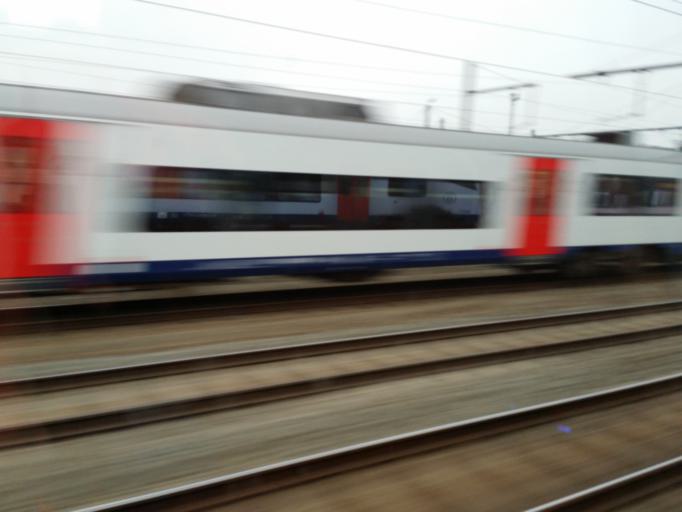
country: BE
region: Flanders
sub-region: Provincie Oost-Vlaanderen
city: Ledeberg
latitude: 51.0229
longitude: 3.7595
